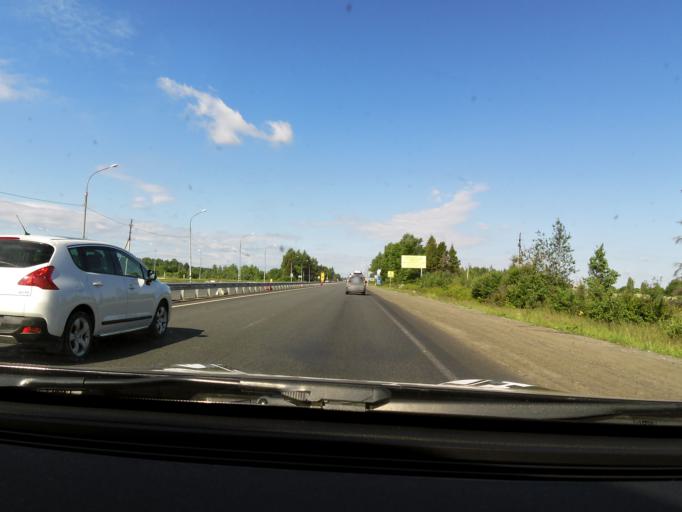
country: RU
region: Tverskaya
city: Emmaus
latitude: 56.7837
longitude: 36.0615
